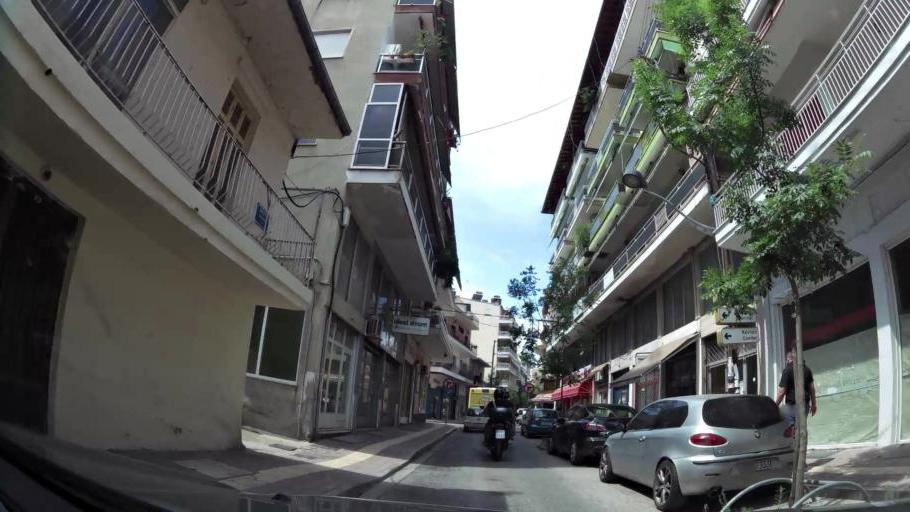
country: GR
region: Central Macedonia
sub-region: Nomos Pierias
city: Katerini
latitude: 40.2739
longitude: 22.5065
